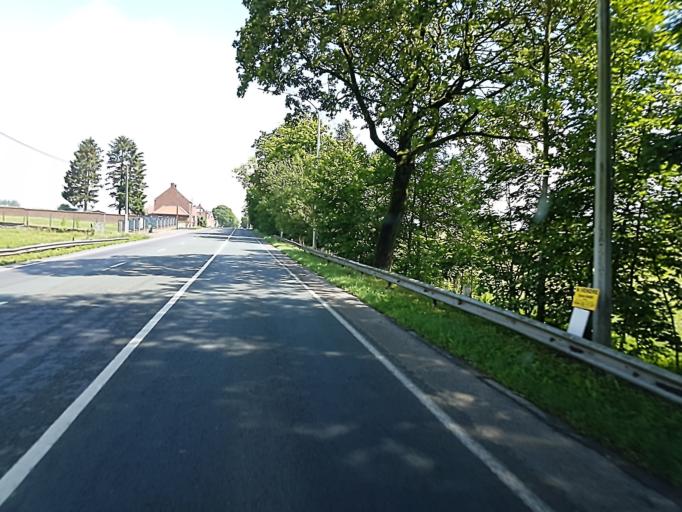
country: BE
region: Wallonia
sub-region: Province du Hainaut
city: Soignies
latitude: 50.5431
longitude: 4.0457
